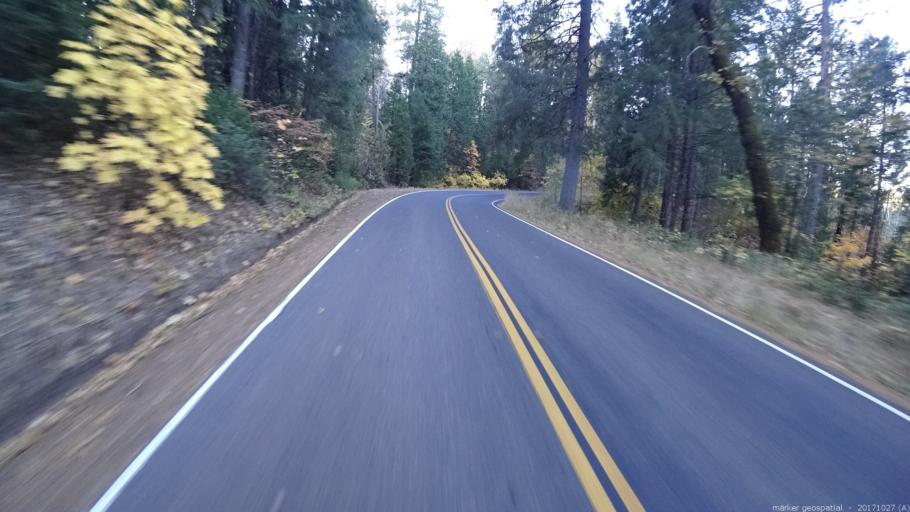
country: US
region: California
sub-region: Shasta County
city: Burney
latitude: 40.8980
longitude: -121.9026
